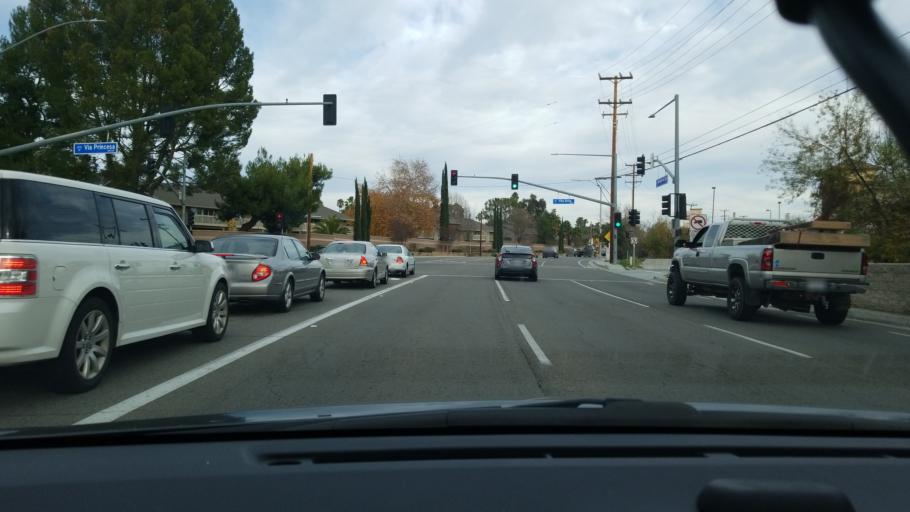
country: US
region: California
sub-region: Riverside County
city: Murrieta Hot Springs
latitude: 33.5568
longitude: -117.1607
